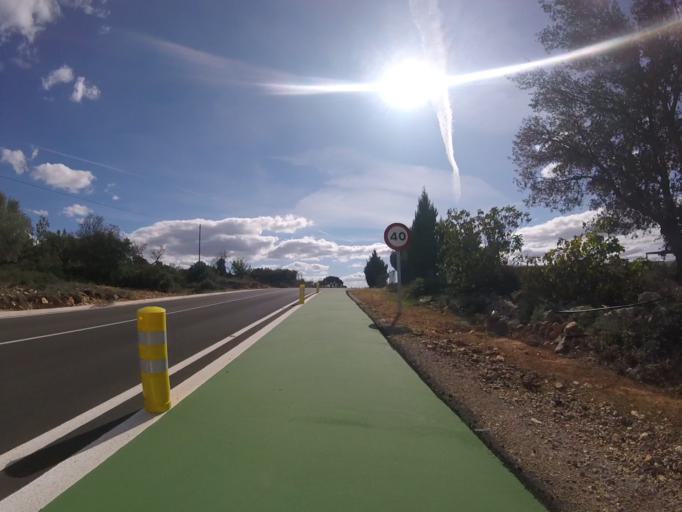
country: ES
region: Valencia
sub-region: Provincia de Castello
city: Albocasser
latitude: 40.4104
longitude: 0.0713
